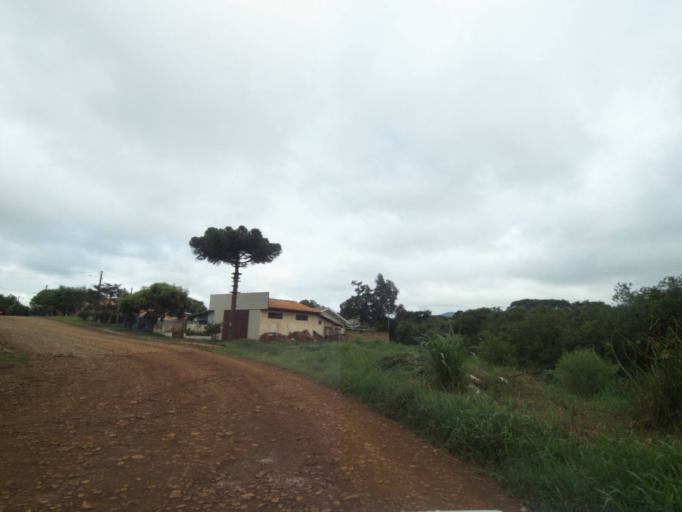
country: BR
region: Parana
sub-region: Pitanga
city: Pitanga
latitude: -24.9359
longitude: -51.8702
